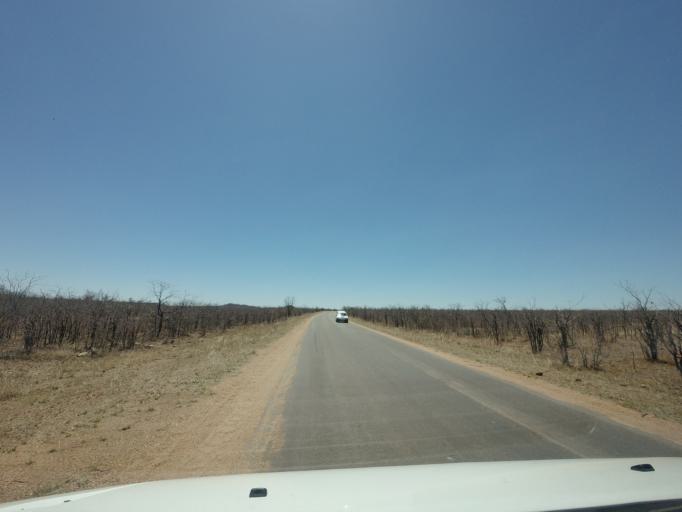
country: ZA
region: Limpopo
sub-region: Mopani District Municipality
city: Phalaborwa
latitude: -23.5367
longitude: 31.4214
